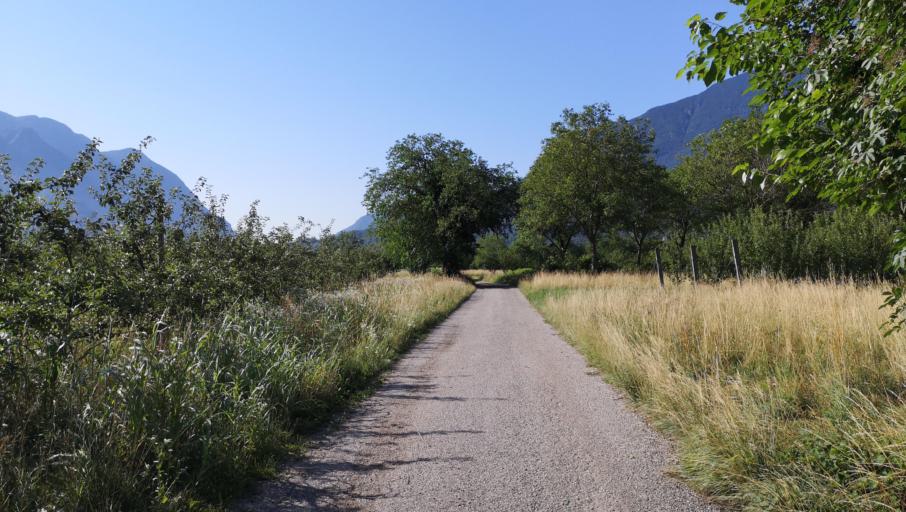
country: IT
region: Friuli Venezia Giulia
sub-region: Provincia di Udine
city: Cavazzo Carnico
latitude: 46.3775
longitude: 13.0407
